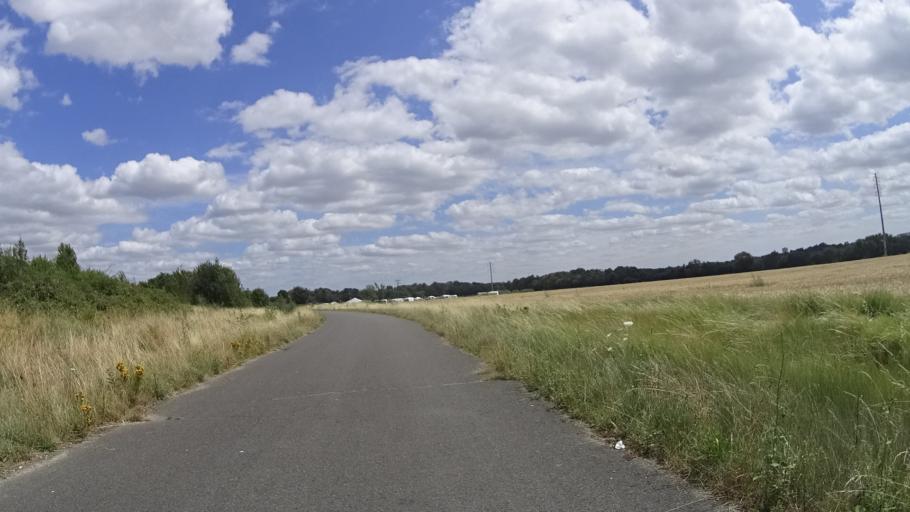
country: FR
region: Centre
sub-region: Departement d'Indre-et-Loire
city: La Riche
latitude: 47.3734
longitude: 0.6545
